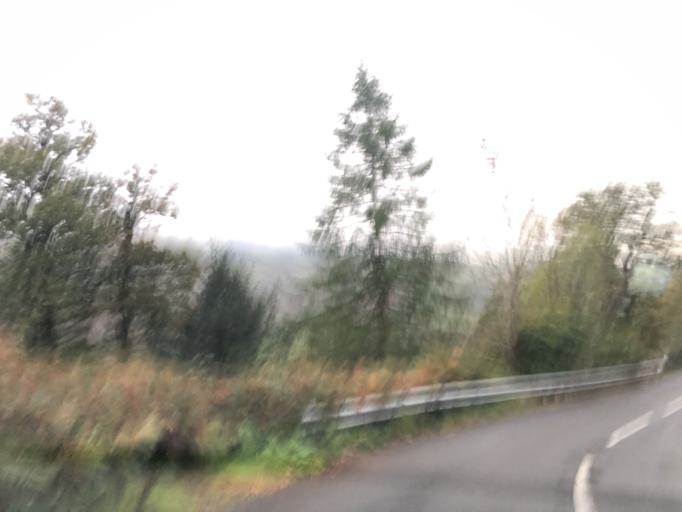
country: GB
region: England
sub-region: Cumbria
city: Windermere
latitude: 54.4338
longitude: -2.9020
